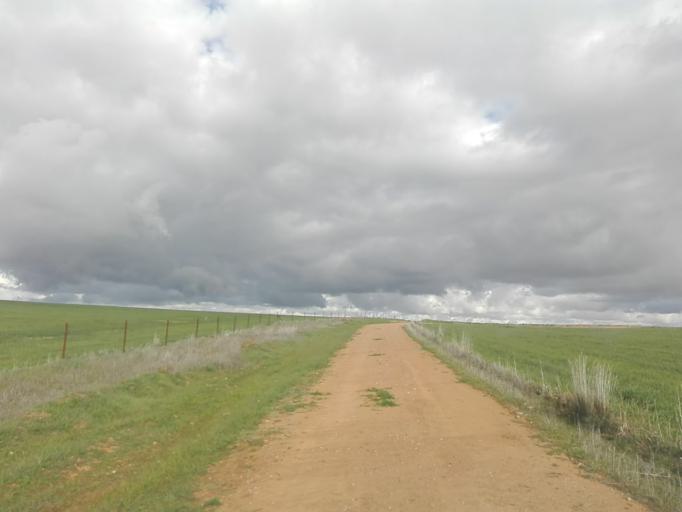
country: ES
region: Extremadura
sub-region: Provincia de Badajoz
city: Llerena
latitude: 38.2872
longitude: -6.0131
